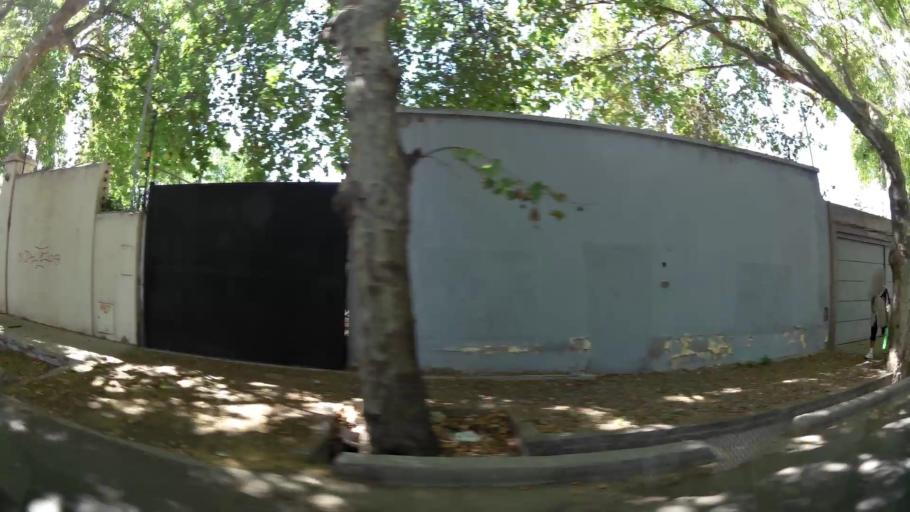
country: AR
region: Mendoza
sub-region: Departamento de Godoy Cruz
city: Godoy Cruz
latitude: -32.9599
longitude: -68.8628
